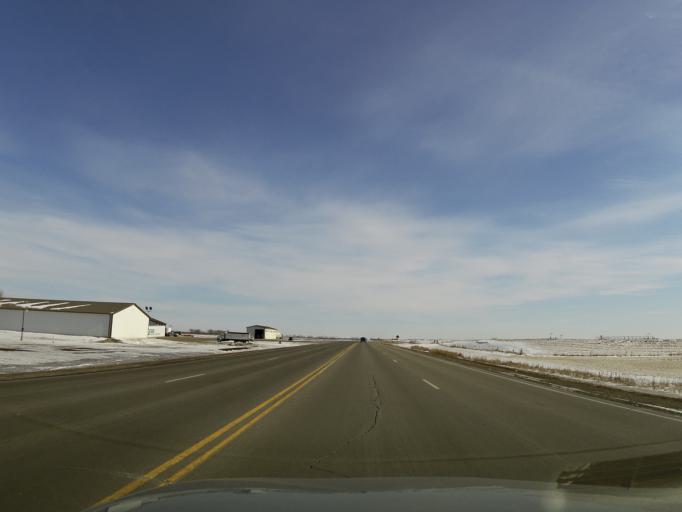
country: US
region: North Dakota
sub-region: Walsh County
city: Grafton
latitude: 48.4125
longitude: -97.3890
